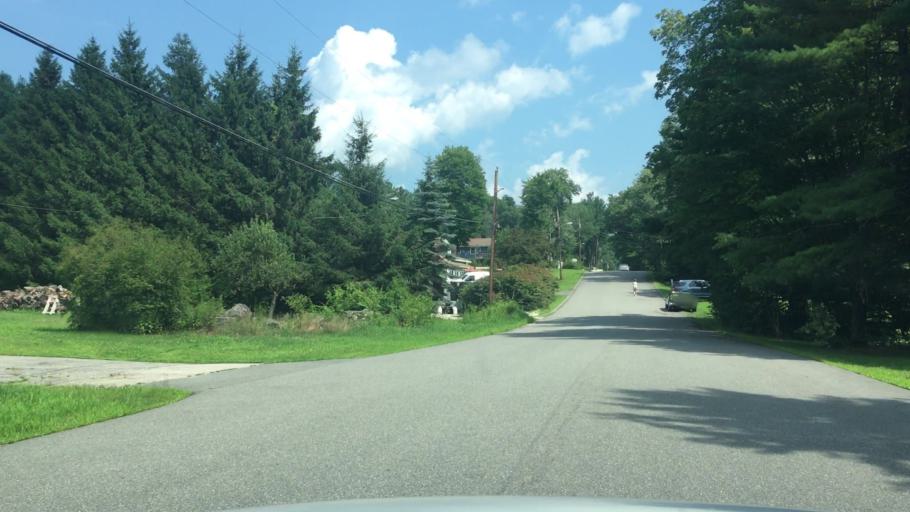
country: US
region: New Hampshire
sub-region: Rockingham County
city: Derry Village
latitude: 42.9345
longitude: -71.3409
